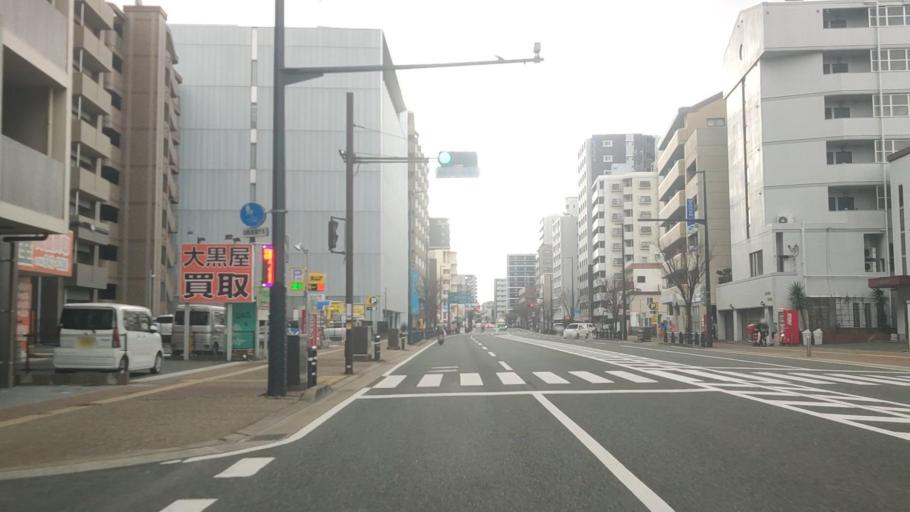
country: JP
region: Fukuoka
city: Fukuoka-shi
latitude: 33.6163
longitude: 130.4259
